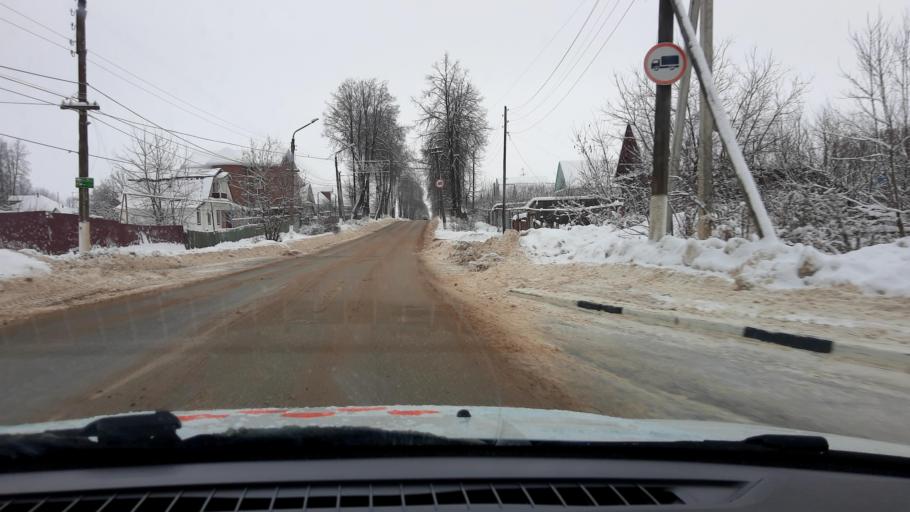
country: RU
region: Nizjnij Novgorod
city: Chkalovsk
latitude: 56.7616
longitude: 43.2406
